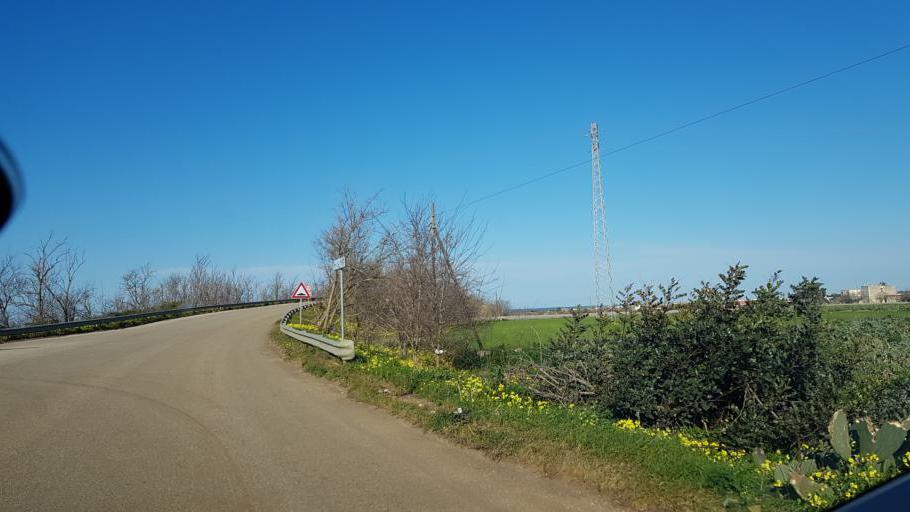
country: IT
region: Apulia
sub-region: Provincia di Brindisi
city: San Vito dei Normanni
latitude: 40.6880
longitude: 17.8228
